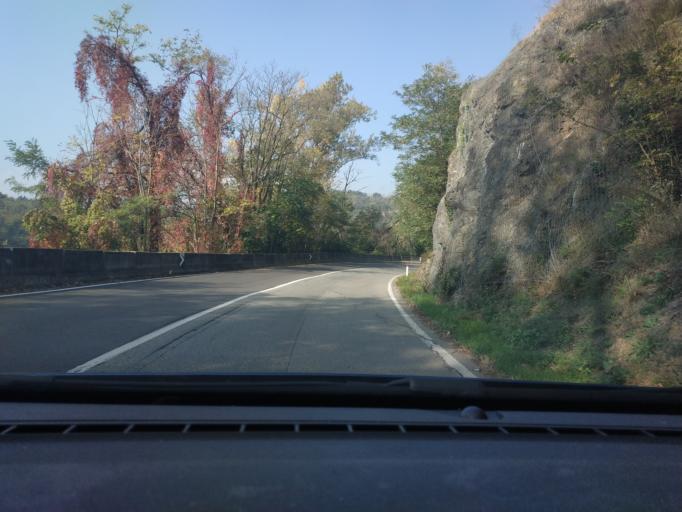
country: IT
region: Piedmont
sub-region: Provincia di Torino
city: Cascinette d'Ivrea
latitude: 45.4853
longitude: 7.9022
